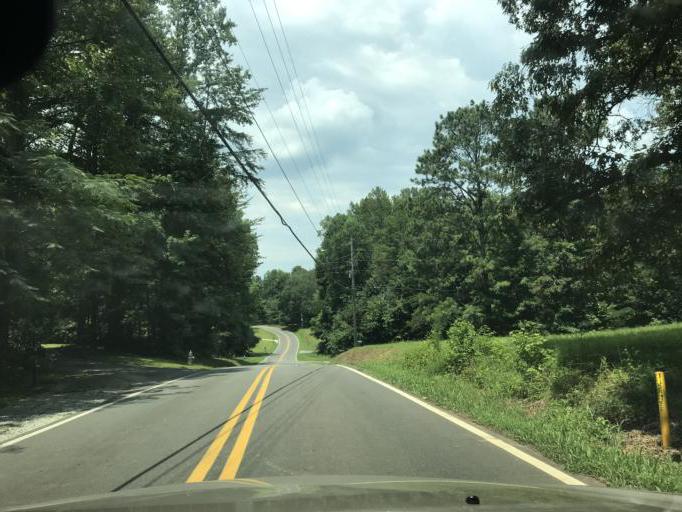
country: US
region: Georgia
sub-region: Dawson County
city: Dawsonville
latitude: 34.3334
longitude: -84.1855
